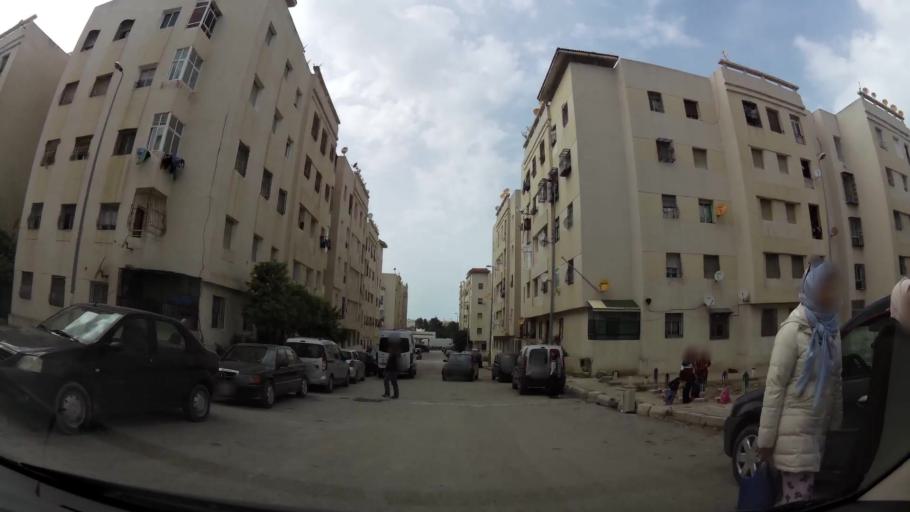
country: MA
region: Tanger-Tetouan
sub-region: Tanger-Assilah
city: Boukhalef
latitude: 35.7340
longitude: -5.8792
